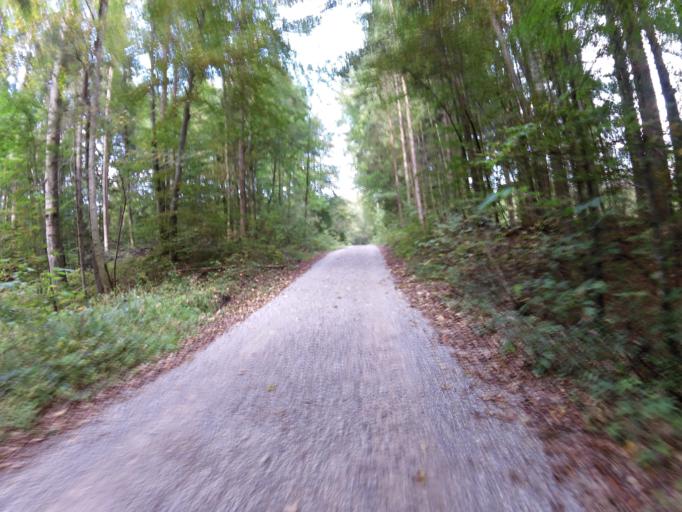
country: DE
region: Bavaria
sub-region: Upper Bavaria
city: Bernried
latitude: 47.8463
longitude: 11.2908
